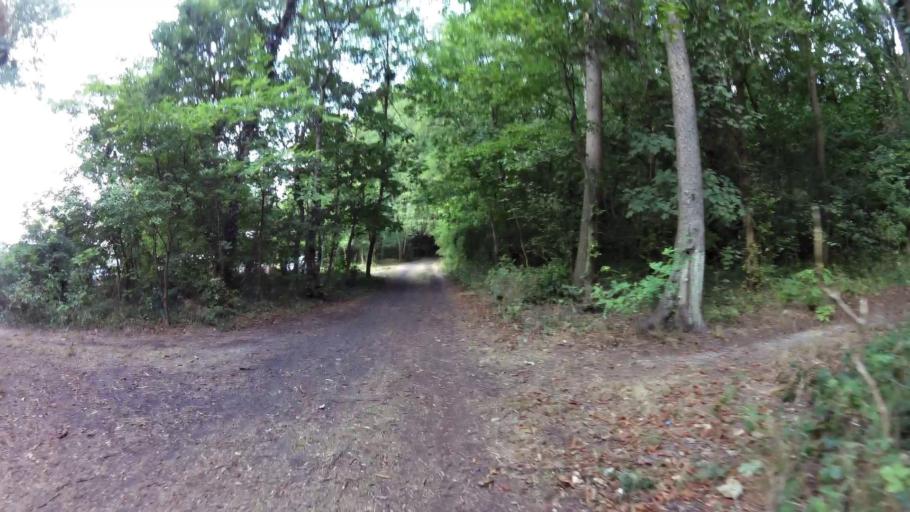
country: PL
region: West Pomeranian Voivodeship
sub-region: Powiat gryfinski
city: Moryn
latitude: 52.8614
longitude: 14.4228
